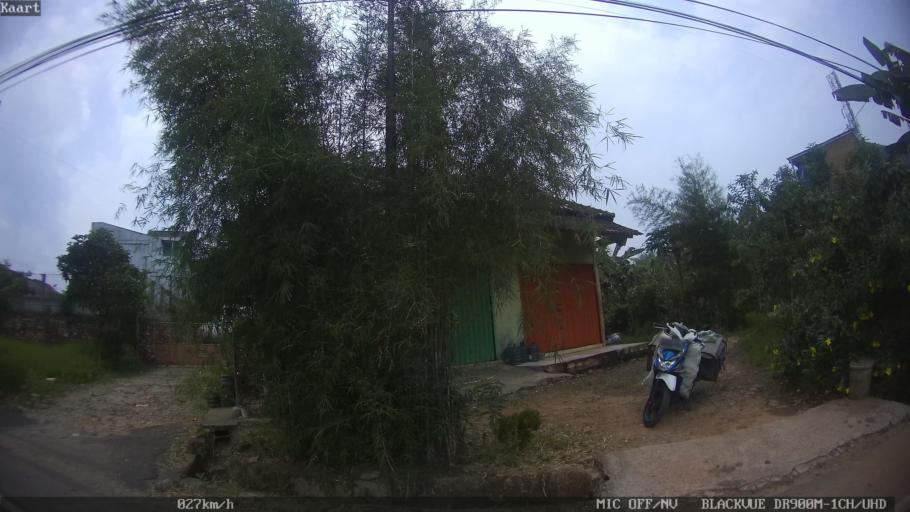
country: ID
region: Lampung
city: Kedaton
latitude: -5.3987
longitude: 105.3169
